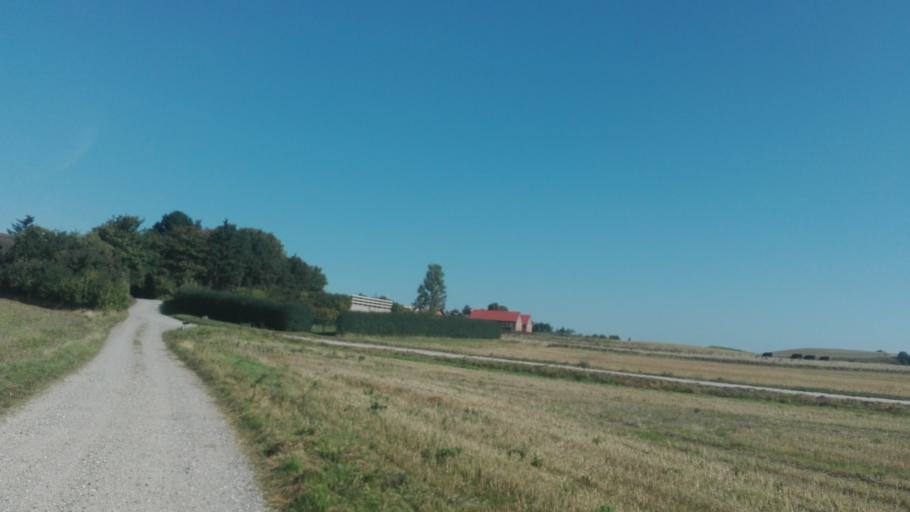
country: DK
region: Central Jutland
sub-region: Syddjurs Kommune
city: Ebeltoft
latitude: 56.2375
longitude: 10.7483
